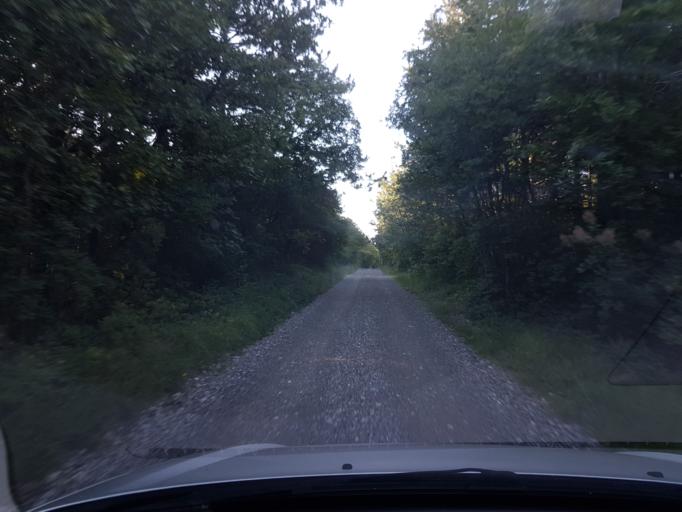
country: SI
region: Sezana
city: Sezana
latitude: 45.7212
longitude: 13.9098
